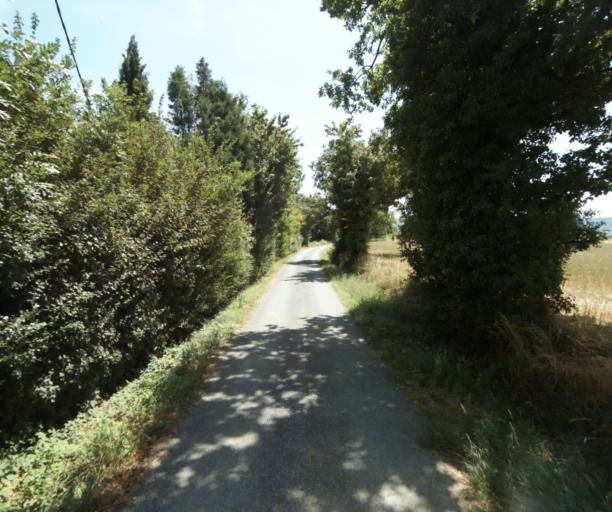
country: FR
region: Midi-Pyrenees
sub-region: Departement du Tarn
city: Soreze
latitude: 43.4898
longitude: 2.0606
